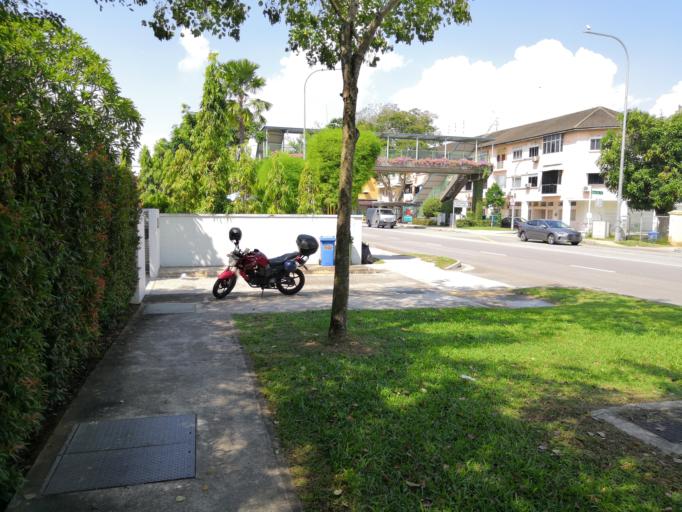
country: SG
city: Singapore
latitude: 1.3086
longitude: 103.9101
